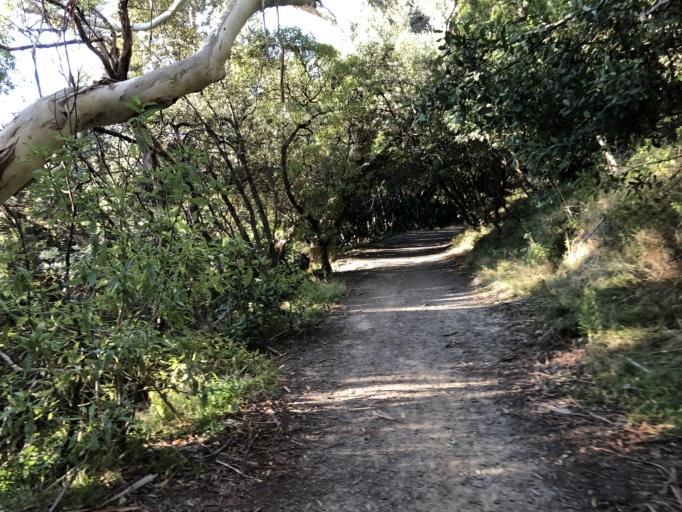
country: NZ
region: Wellington
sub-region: Wellington City
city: Wellington
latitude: -41.2980
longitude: 174.7903
